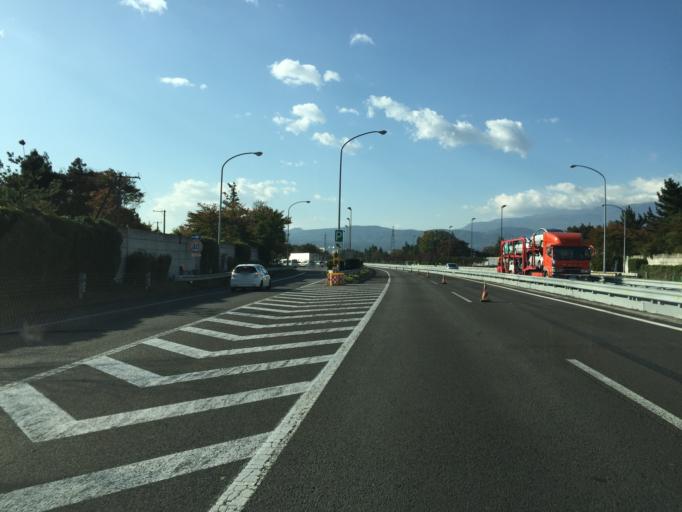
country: JP
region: Fukushima
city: Fukushima-shi
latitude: 37.7617
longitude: 140.4093
